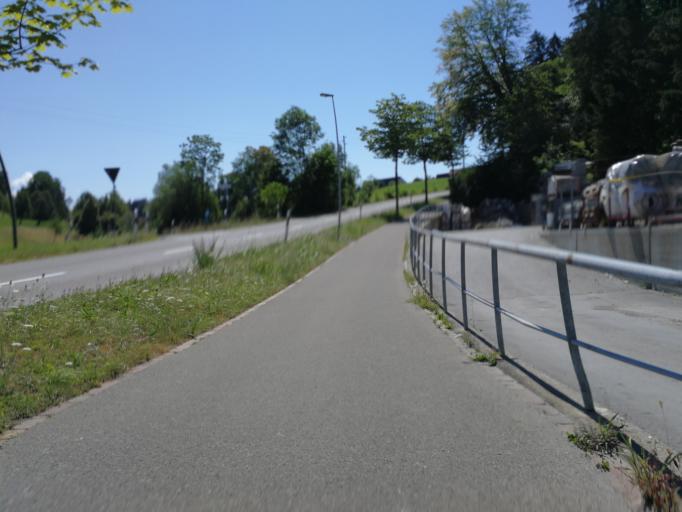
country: CH
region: Zurich
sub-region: Bezirk Uster
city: Uster / Nossikon
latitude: 47.3314
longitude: 8.7429
